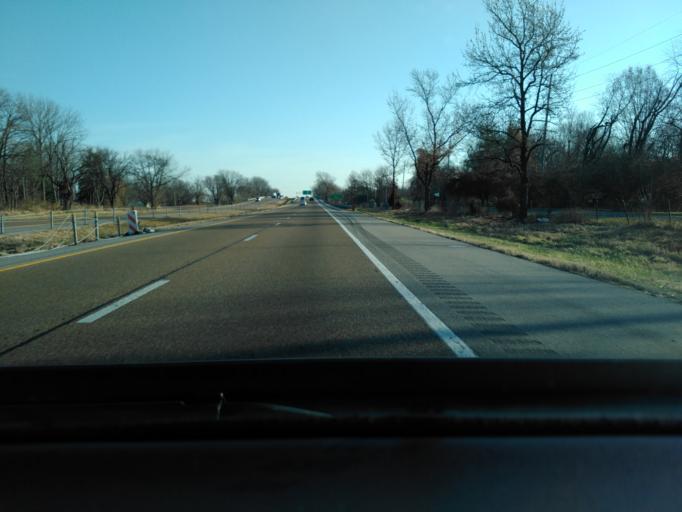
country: US
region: Illinois
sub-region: Madison County
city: Maryville
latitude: 38.7124
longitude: -89.9335
